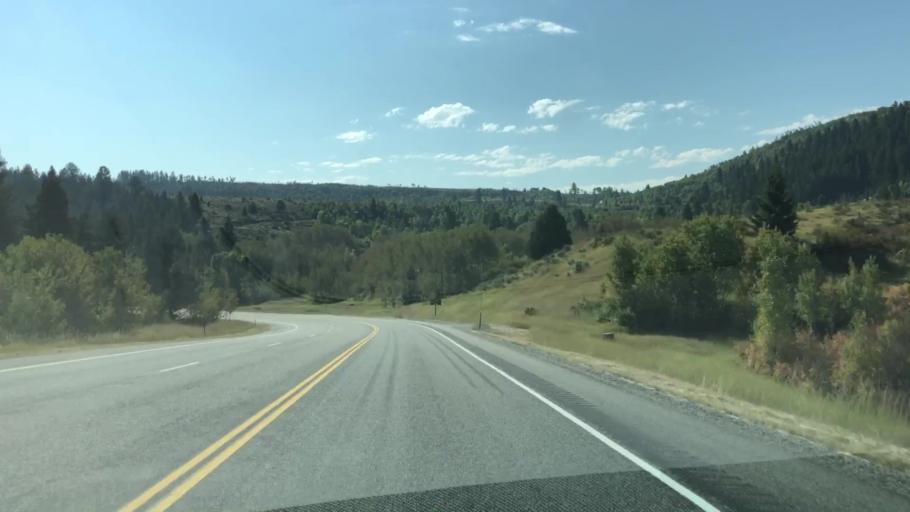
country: US
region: Idaho
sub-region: Teton County
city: Victor
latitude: 43.4521
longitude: -111.4043
